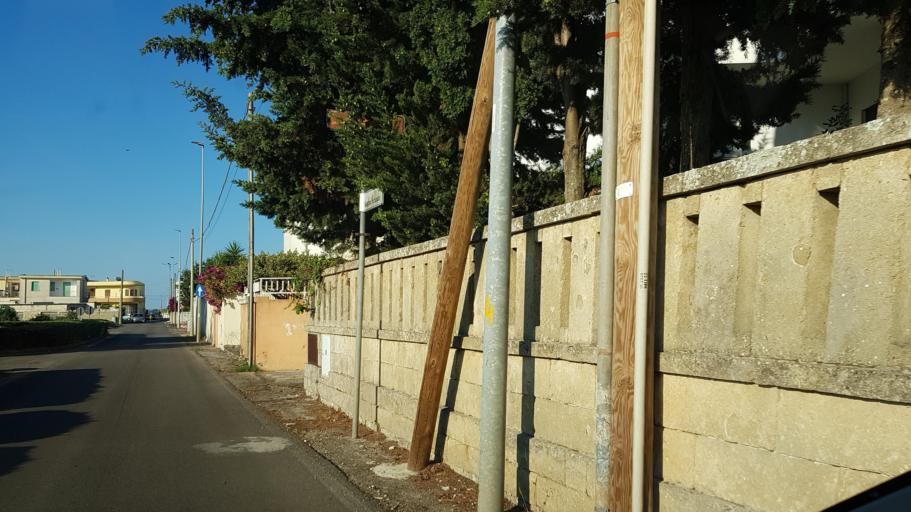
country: IT
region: Apulia
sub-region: Provincia di Lecce
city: Marittima
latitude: 39.9984
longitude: 18.3938
